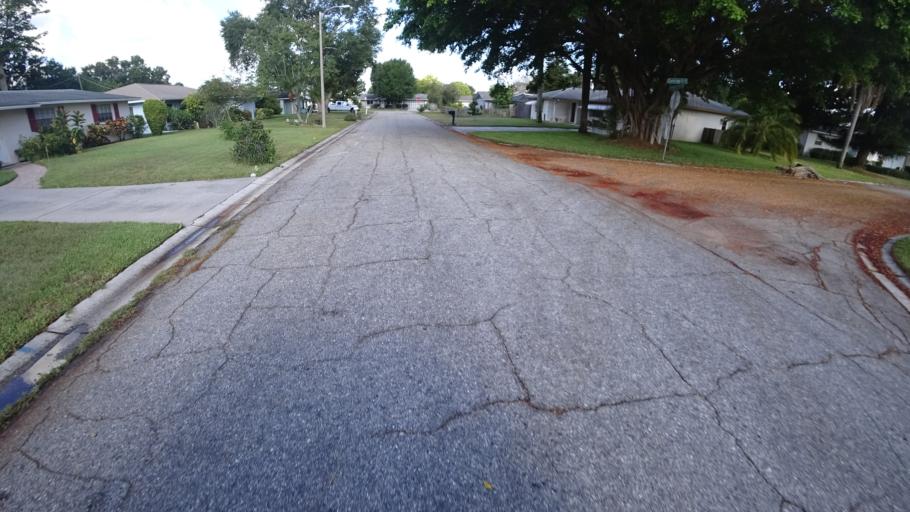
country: US
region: Florida
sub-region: Manatee County
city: South Bradenton
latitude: 27.4728
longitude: -82.5946
